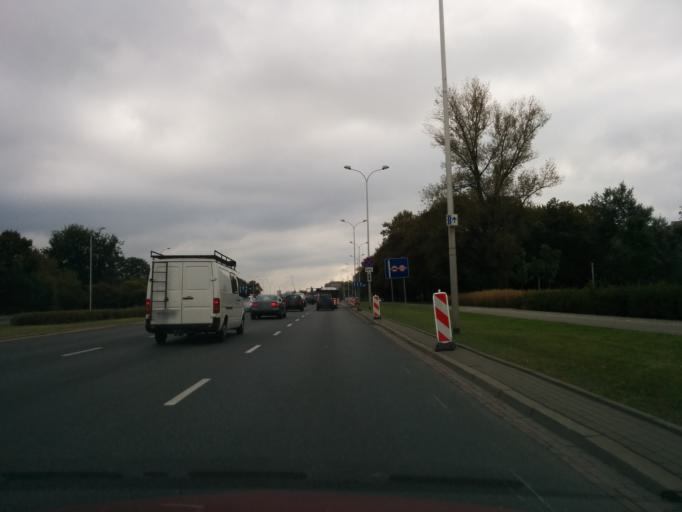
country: PL
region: Masovian Voivodeship
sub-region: Warszawa
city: Praga Polnoc
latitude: 52.2544
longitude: 21.0121
